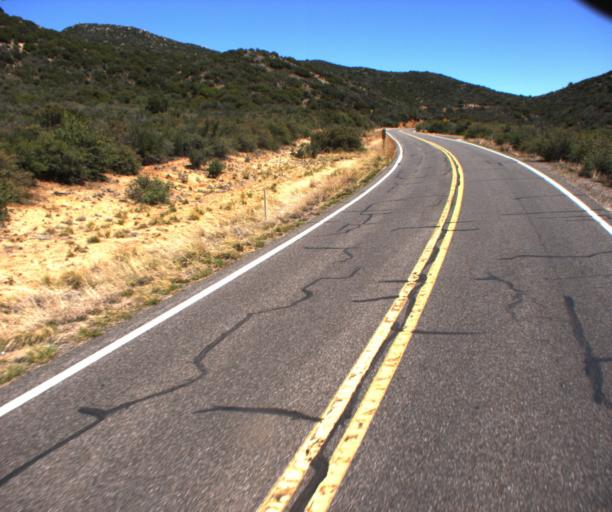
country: US
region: Arizona
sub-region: Yavapai County
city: Prescott
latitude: 34.4239
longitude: -112.5571
